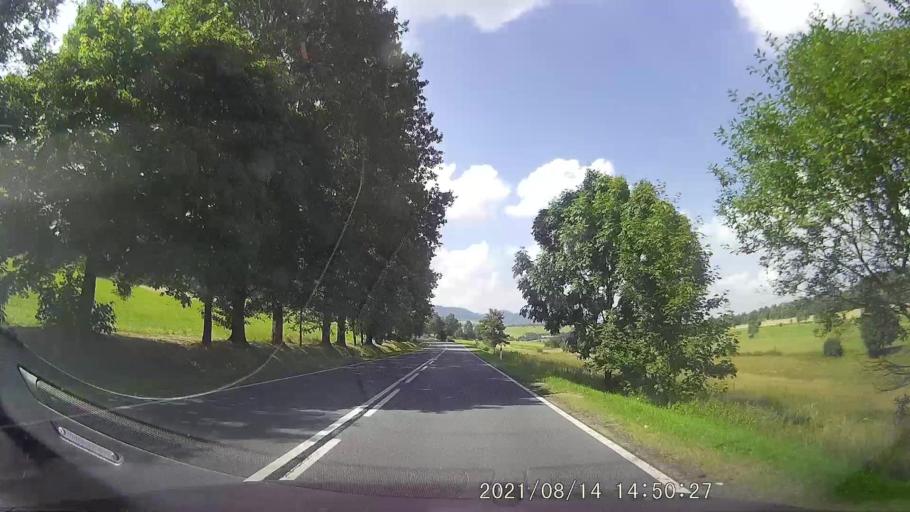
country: PL
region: Lower Silesian Voivodeship
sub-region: Powiat walbrzyski
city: Gluszyca Gorna
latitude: 50.6521
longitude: 16.3800
